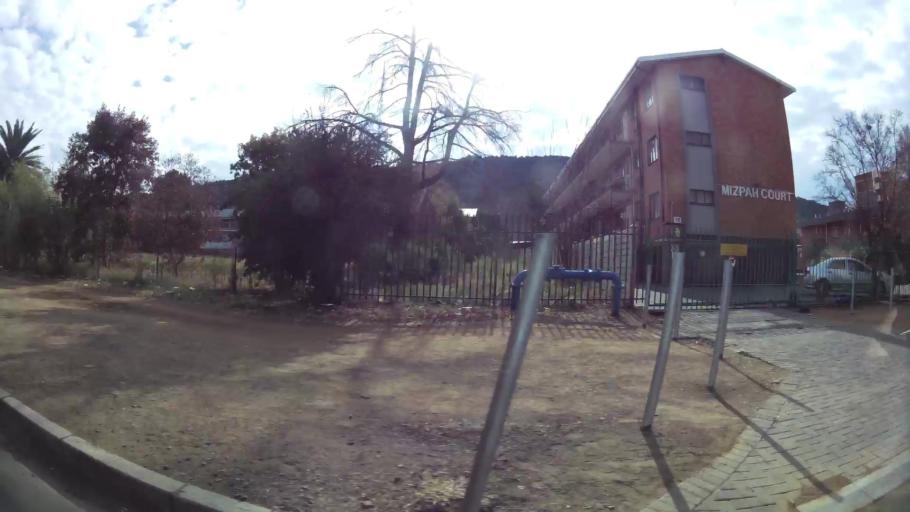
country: ZA
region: Orange Free State
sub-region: Mangaung Metropolitan Municipality
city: Bloemfontein
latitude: -29.1074
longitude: 26.2345
